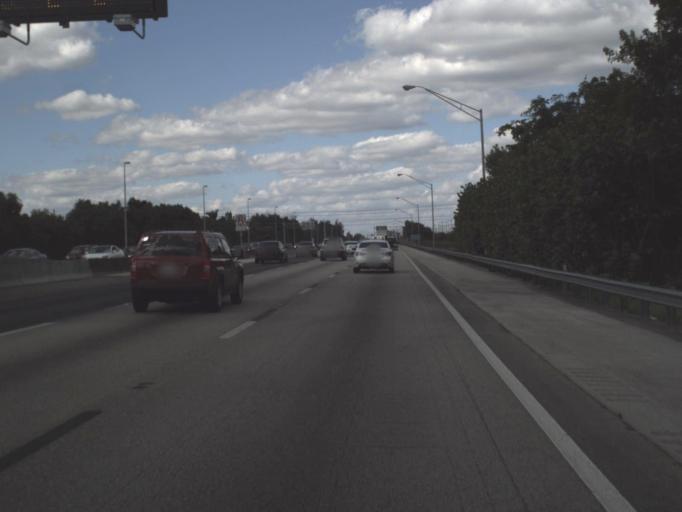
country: US
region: Florida
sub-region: Broward County
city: Davie
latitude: 26.0522
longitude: -80.2148
